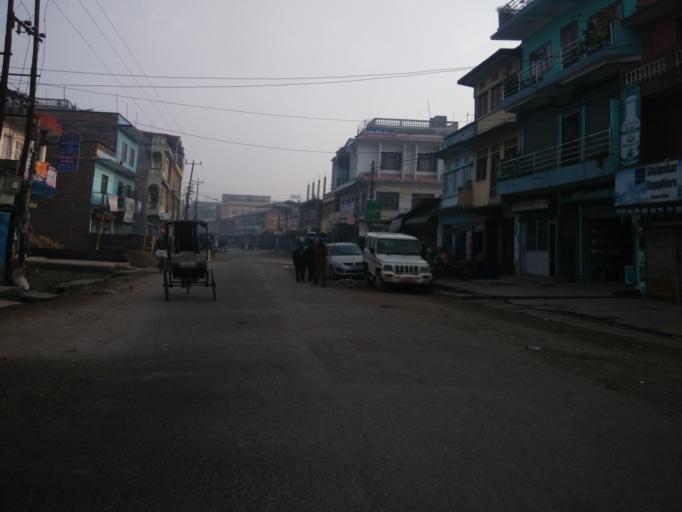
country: NP
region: Central Region
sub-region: Narayani Zone
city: Bharatpur
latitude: 27.6921
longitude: 84.4214
